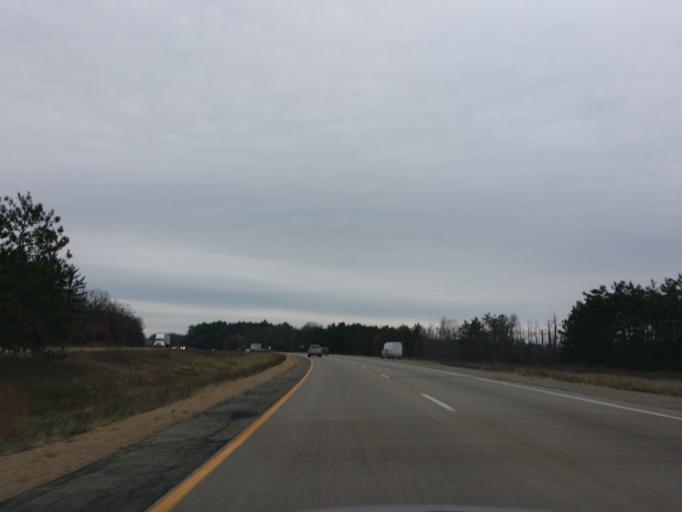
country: US
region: Wisconsin
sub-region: Columbia County
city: Wisconsin Dells
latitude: 43.6496
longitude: -89.8133
